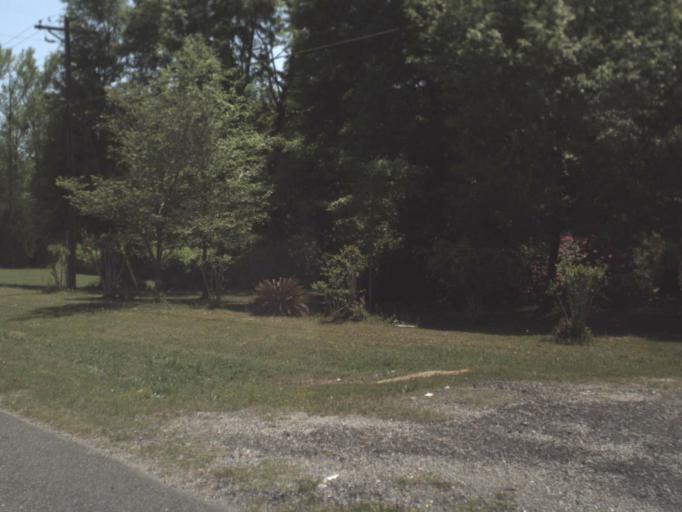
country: US
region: Florida
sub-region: Escambia County
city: Century
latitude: 30.9517
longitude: -87.2004
